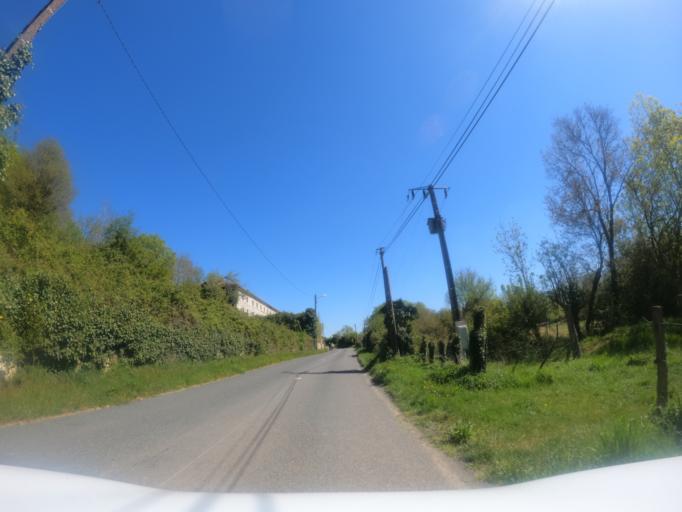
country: FR
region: Pays de la Loire
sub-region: Departement de la Vendee
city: Fontenay-le-Comte
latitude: 46.4433
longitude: -0.8513
